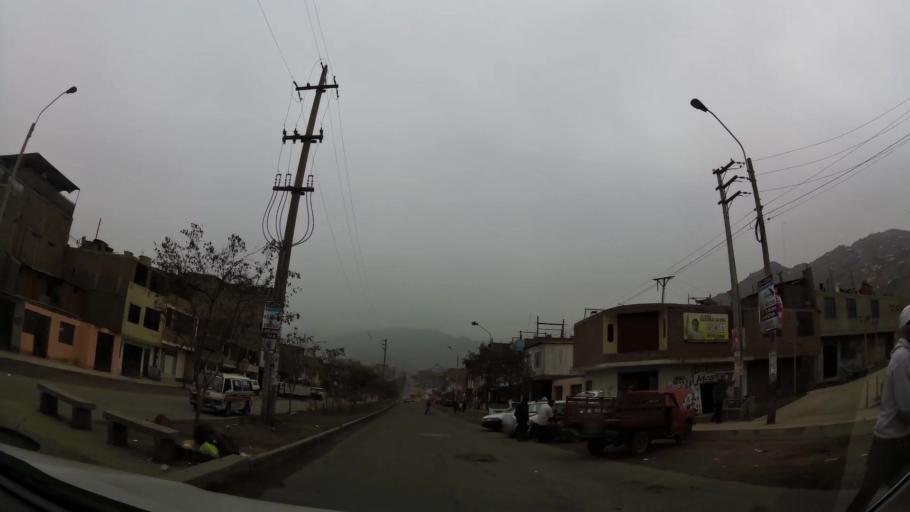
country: PE
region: Lima
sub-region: Lima
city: Independencia
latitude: -11.9423
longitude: -76.9837
